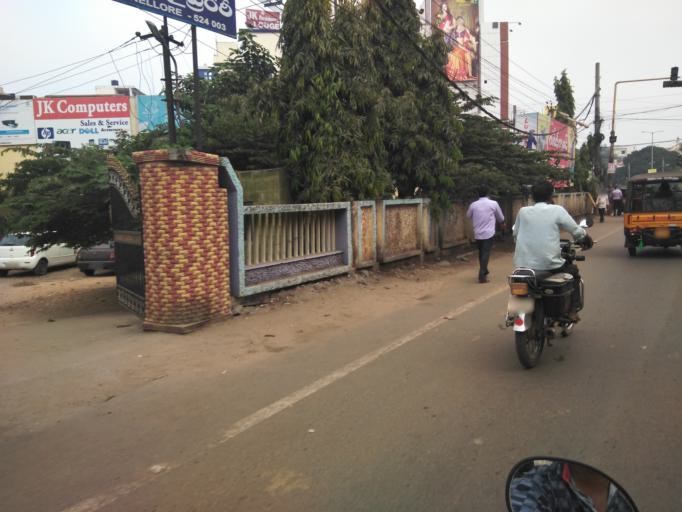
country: IN
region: Andhra Pradesh
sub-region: Nellore
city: Nellore
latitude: 14.4471
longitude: 79.9816
